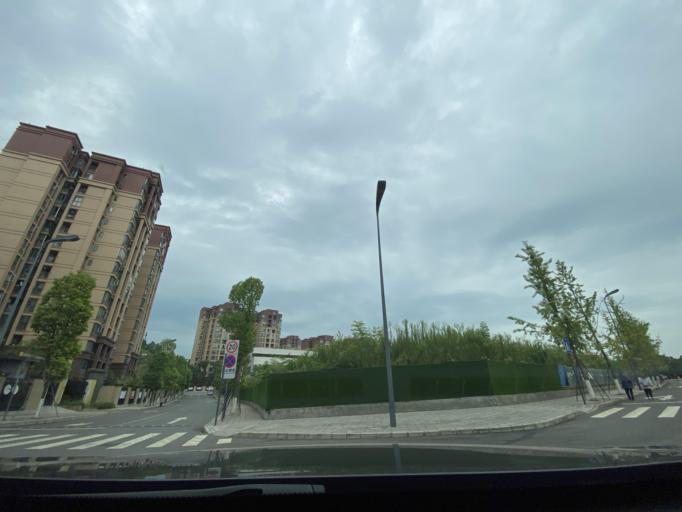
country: CN
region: Sichuan
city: Jiancheng
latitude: 30.3294
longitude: 104.4896
